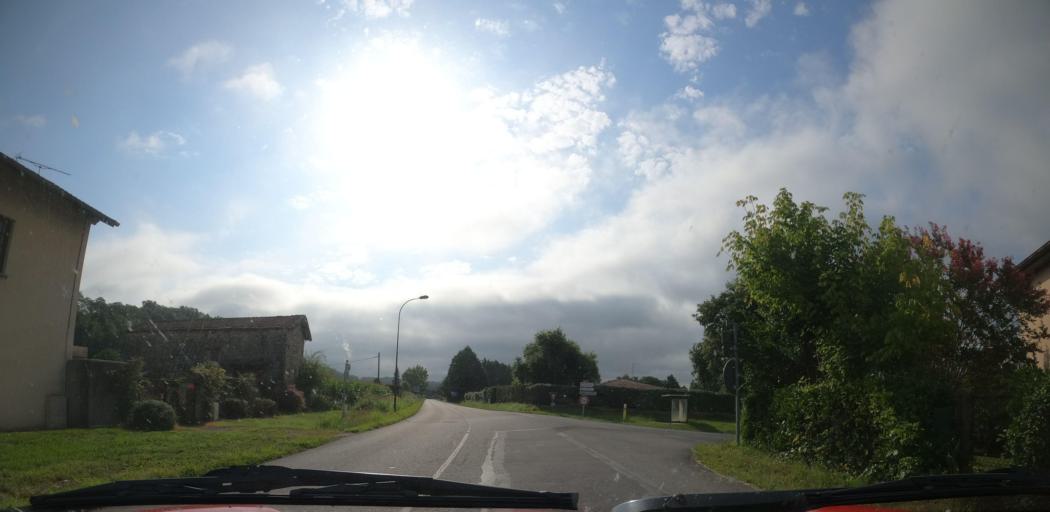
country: FR
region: Aquitaine
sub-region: Departement des Landes
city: Peyrehorade
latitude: 43.5329
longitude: -1.0668
